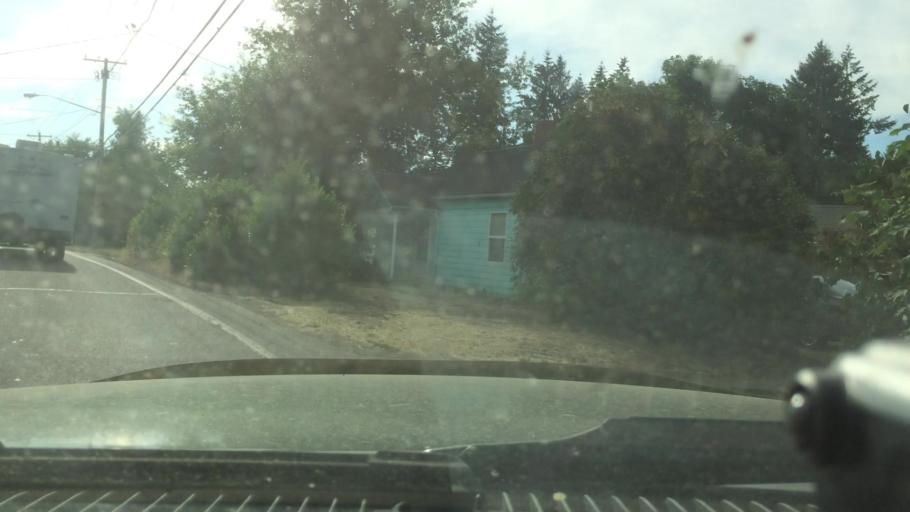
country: US
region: Oregon
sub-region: Lane County
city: Eugene
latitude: 44.1035
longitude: -123.1200
